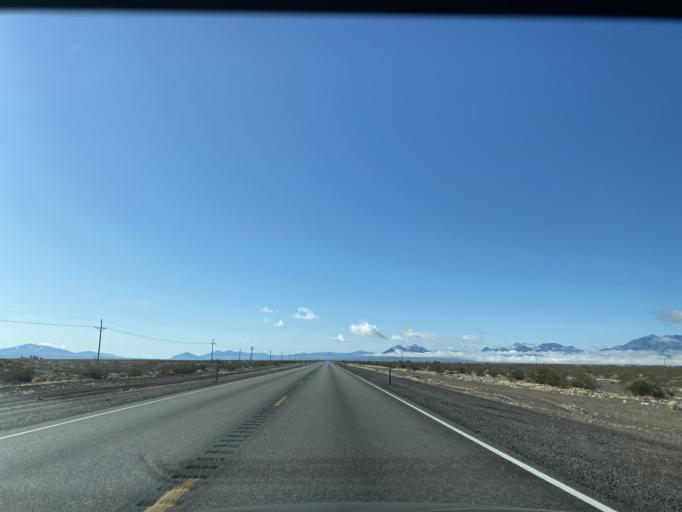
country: US
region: Nevada
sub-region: Nye County
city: Beatty
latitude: 36.5875
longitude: -116.4104
